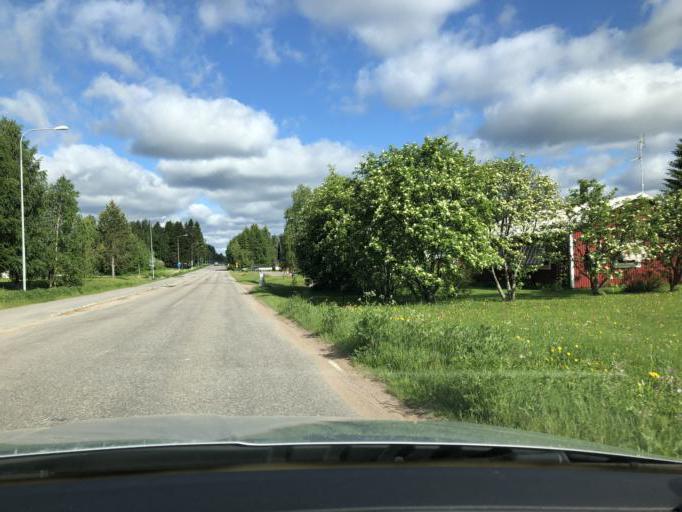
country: SE
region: Norrbotten
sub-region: Pajala Kommun
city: Pajala
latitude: 67.2181
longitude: 23.3563
